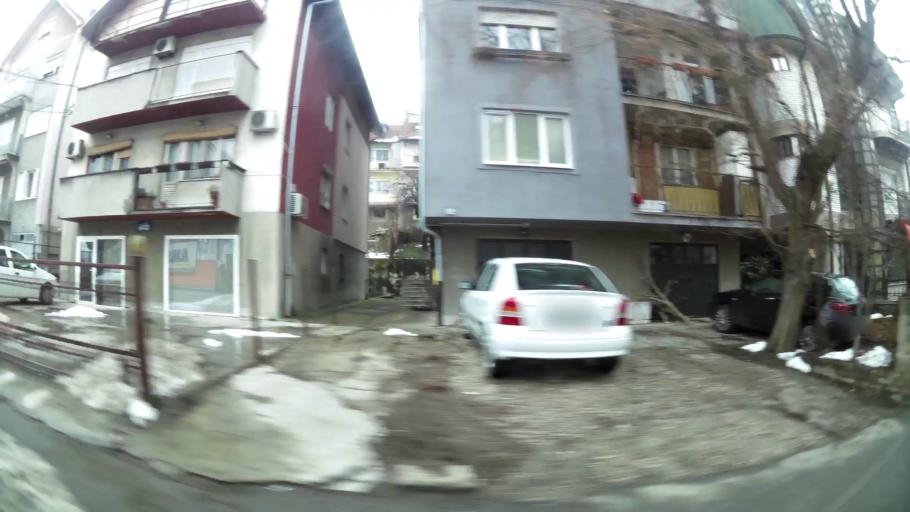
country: RS
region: Central Serbia
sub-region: Belgrade
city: Vozdovac
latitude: 44.7744
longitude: 20.4817
